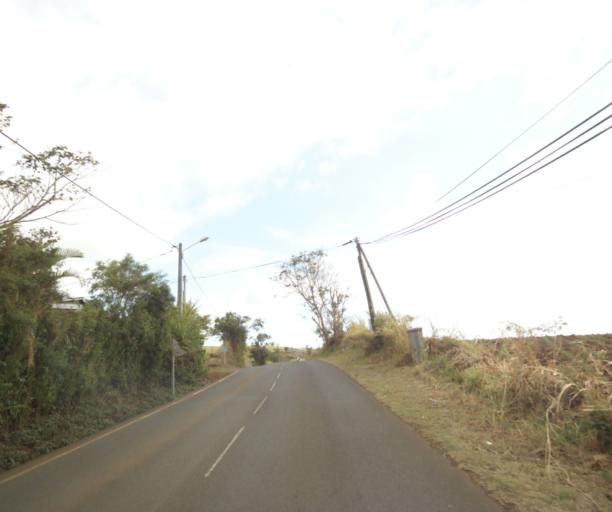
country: RE
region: Reunion
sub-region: Reunion
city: Trois-Bassins
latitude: -21.0697
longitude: 55.2779
